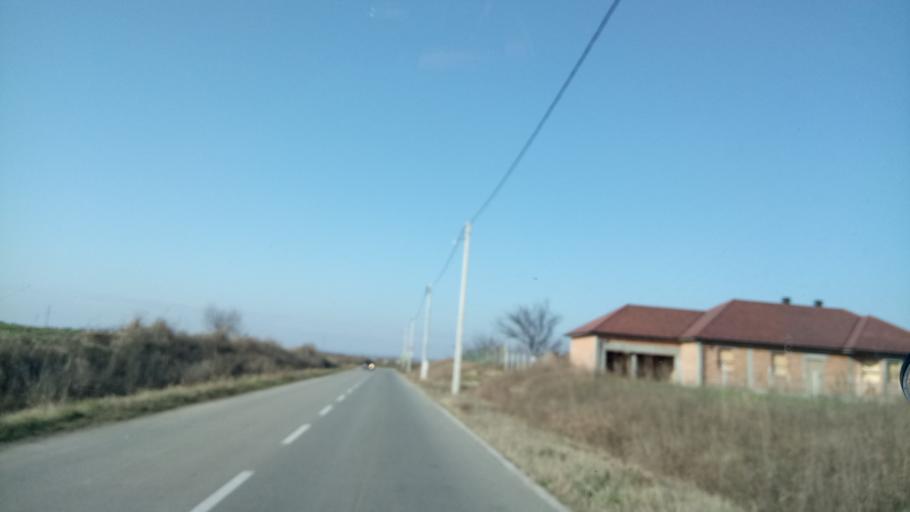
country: RS
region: Autonomna Pokrajina Vojvodina
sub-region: Sremski Okrug
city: Ingija
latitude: 45.0542
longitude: 20.0615
